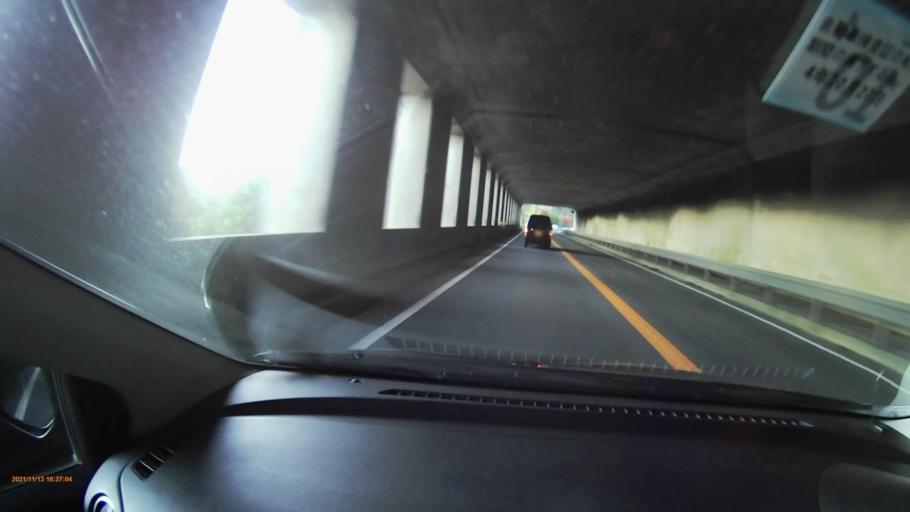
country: JP
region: Gifu
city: Nakatsugawa
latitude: 35.5800
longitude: 137.5385
